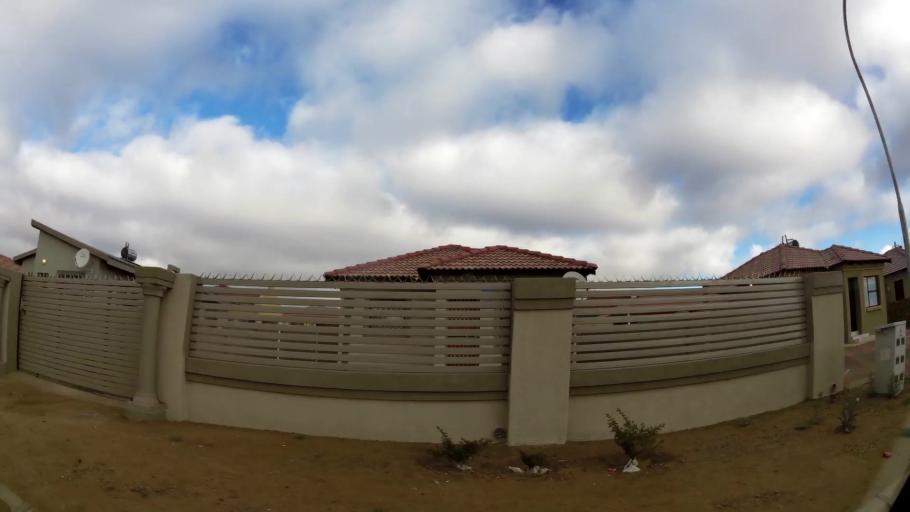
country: ZA
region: Limpopo
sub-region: Capricorn District Municipality
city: Polokwane
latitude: -23.9212
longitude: 29.4463
